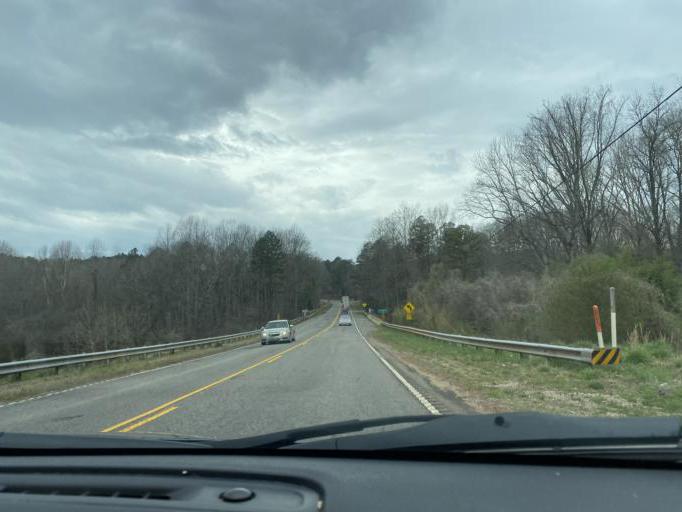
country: US
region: South Carolina
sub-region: Spartanburg County
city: Cowpens
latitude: 35.0168
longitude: -81.7412
